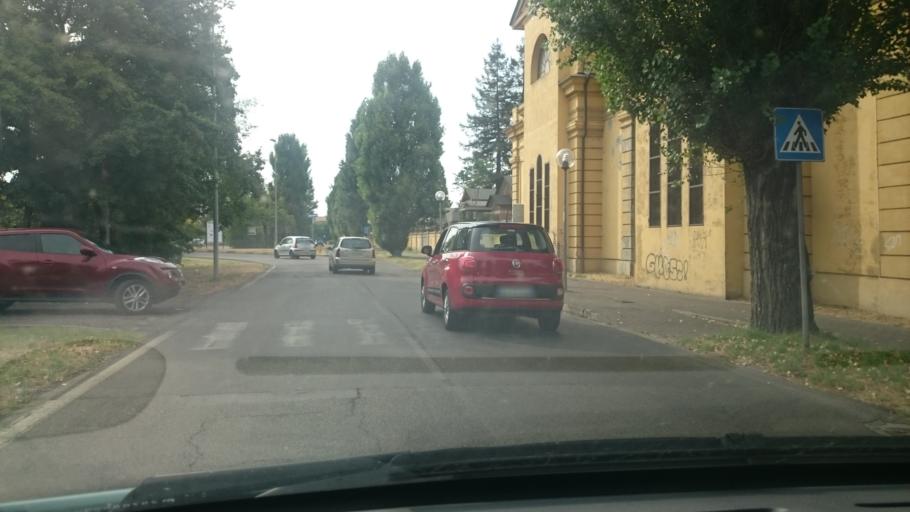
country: IT
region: Emilia-Romagna
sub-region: Provincia di Reggio Emilia
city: Reggio nell'Emilia
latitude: 44.6910
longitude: 10.6232
